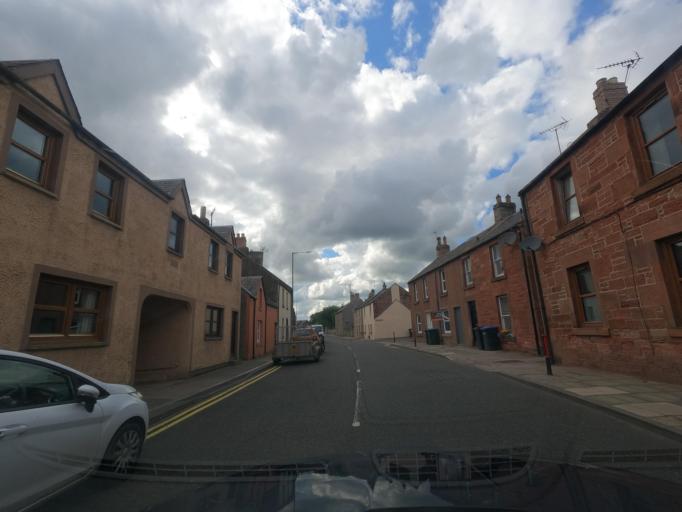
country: GB
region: Scotland
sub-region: The Scottish Borders
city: Kelso
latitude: 55.7069
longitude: -2.4583
